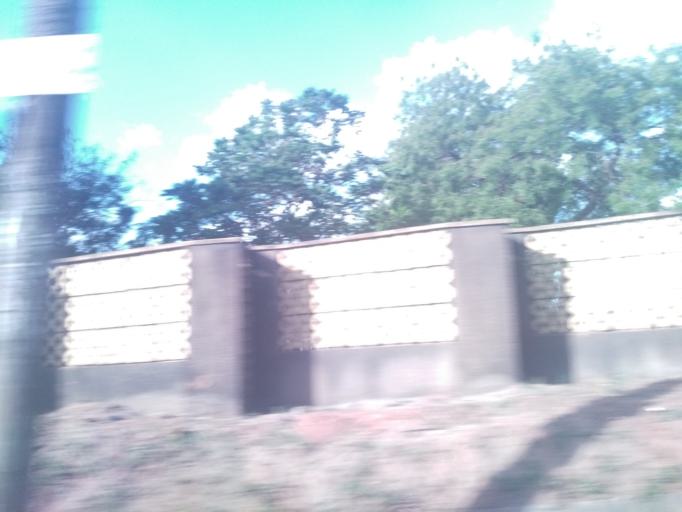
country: TZ
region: Dar es Salaam
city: Dar es Salaam
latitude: -6.8632
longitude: 39.2599
